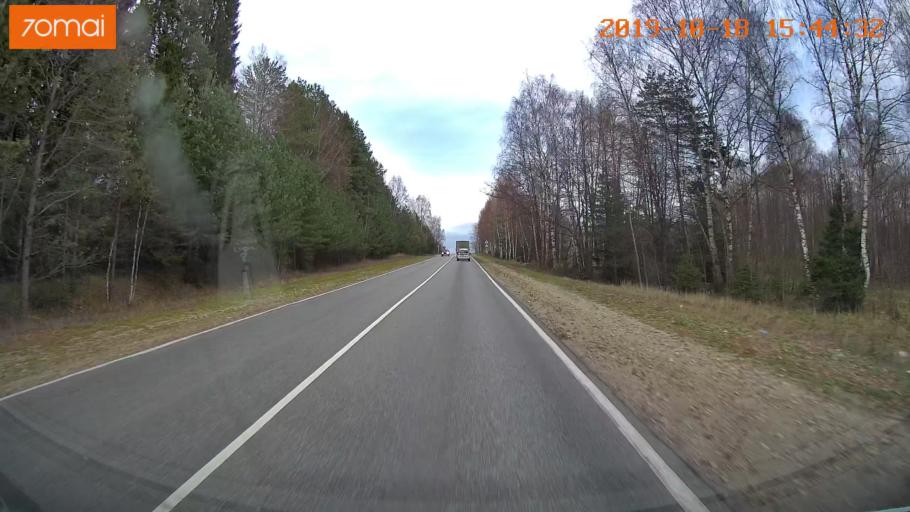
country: RU
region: Vladimir
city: Golovino
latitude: 55.9827
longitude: 40.5516
